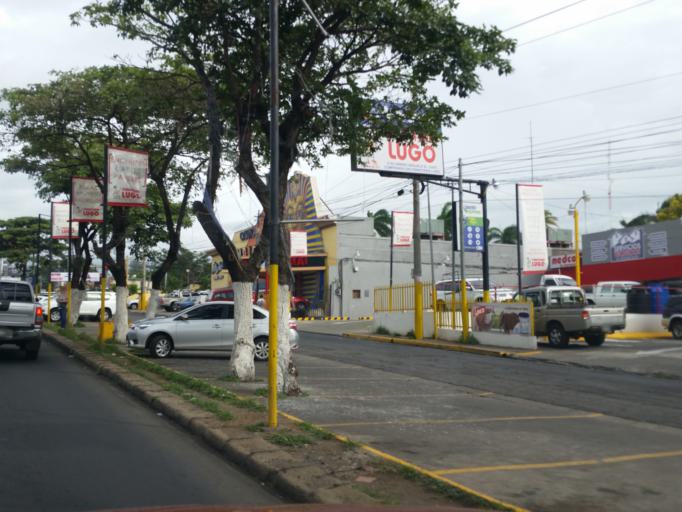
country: NI
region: Managua
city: Managua
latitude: 12.1200
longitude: -86.2615
